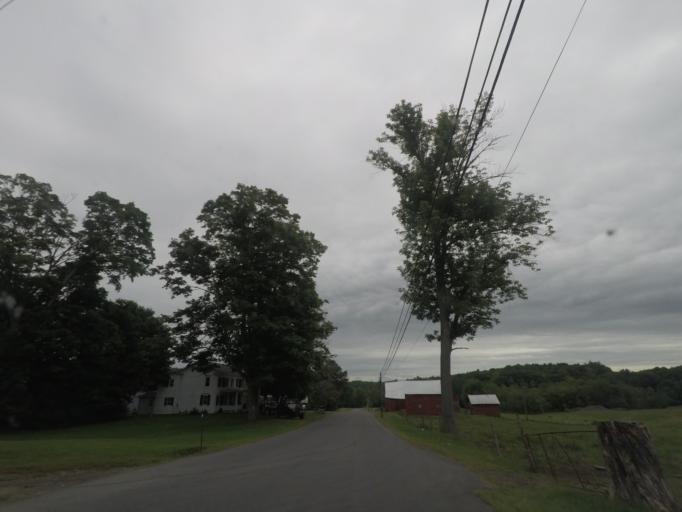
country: US
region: New York
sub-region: Rensselaer County
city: Nassau
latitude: 42.4928
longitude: -73.6008
